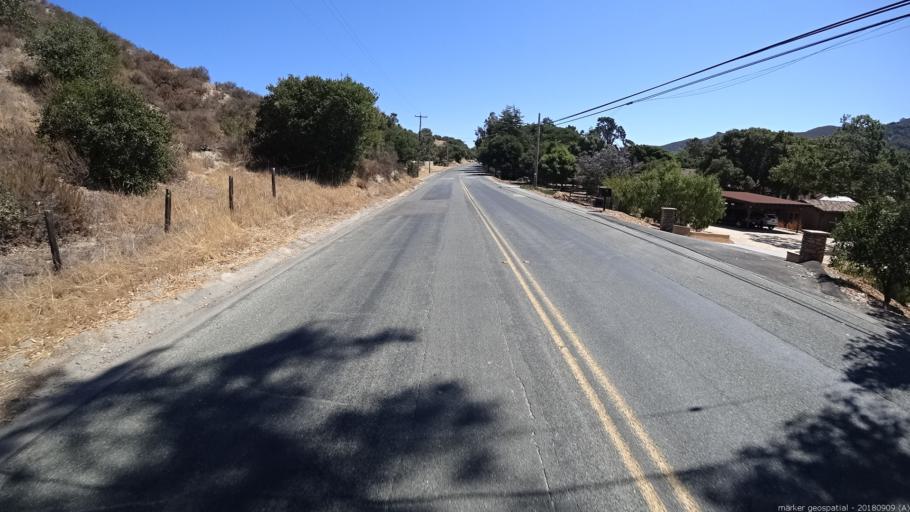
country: US
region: California
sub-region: Monterey County
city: Carmel Valley Village
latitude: 36.5752
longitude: -121.7150
